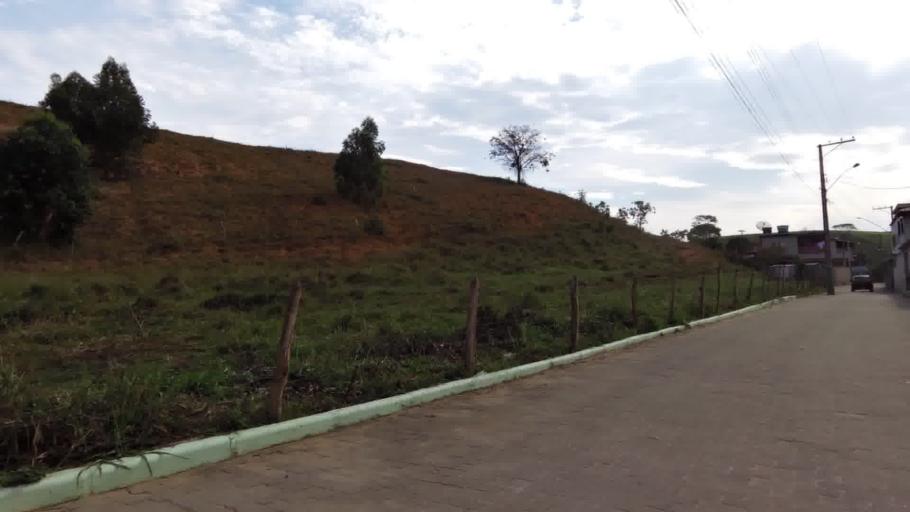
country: BR
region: Espirito Santo
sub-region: Piuma
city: Piuma
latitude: -20.8366
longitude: -40.7343
